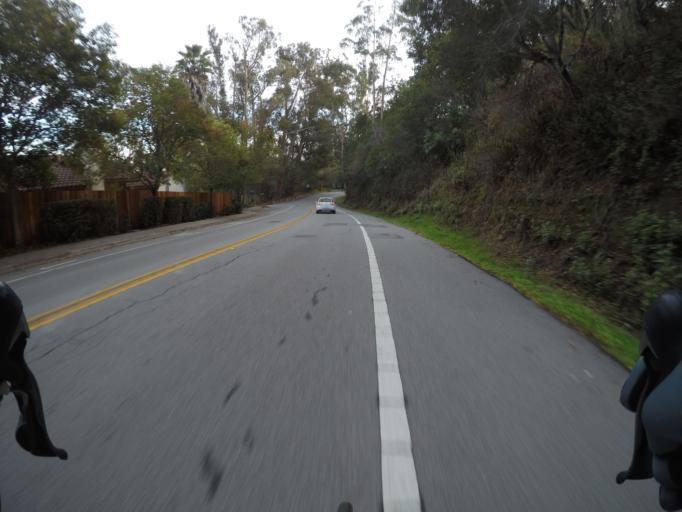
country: US
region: California
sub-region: Santa Cruz County
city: Soquel
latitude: 36.9842
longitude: -121.9606
